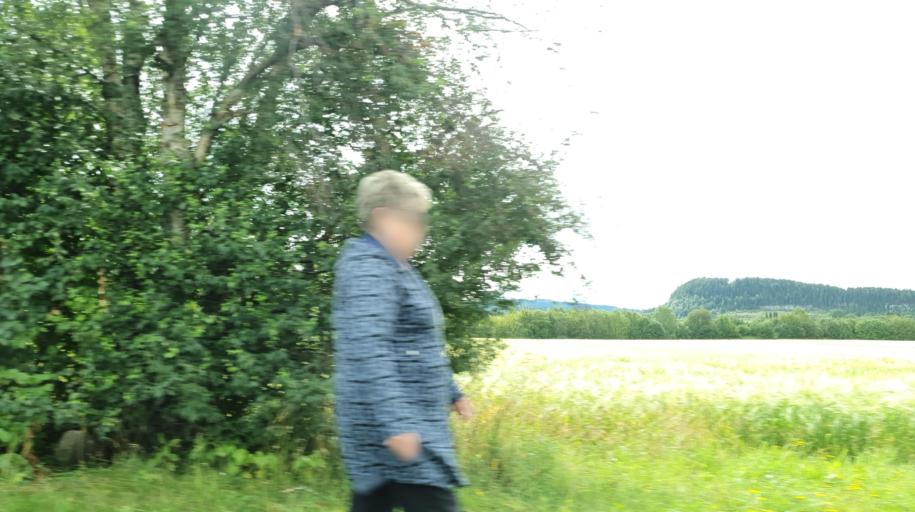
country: NO
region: Nord-Trondelag
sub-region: Stjordal
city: Stjordalshalsen
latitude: 63.4522
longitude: 10.9708
